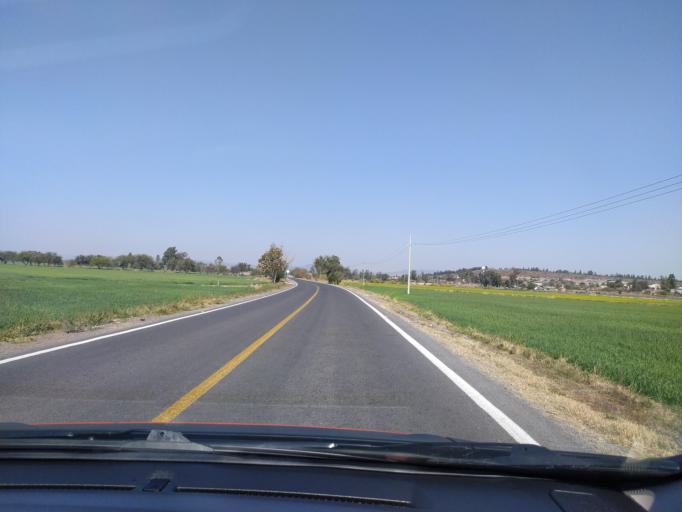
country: MX
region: Guanajuato
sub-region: San Francisco del Rincon
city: San Ignacio de Hidalgo
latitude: 20.8490
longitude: -101.8507
